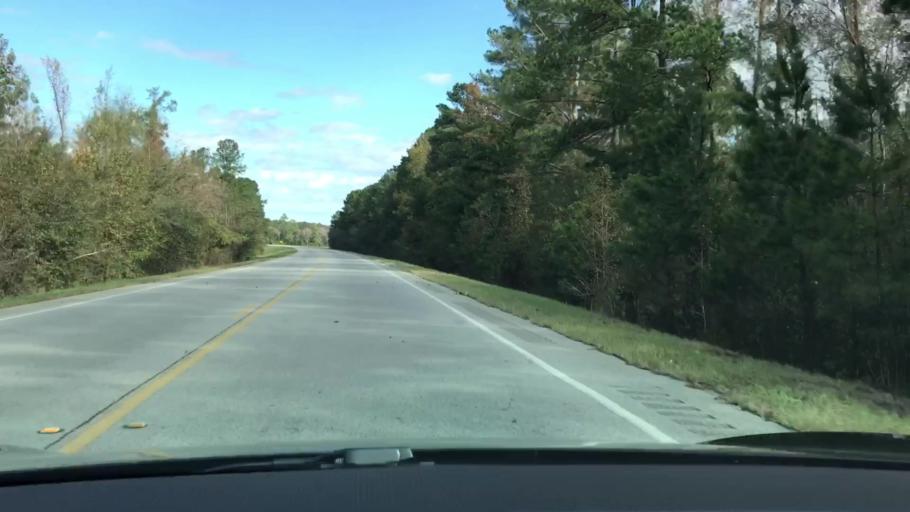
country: US
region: Georgia
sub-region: Jefferson County
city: Louisville
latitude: 32.9583
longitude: -82.3919
